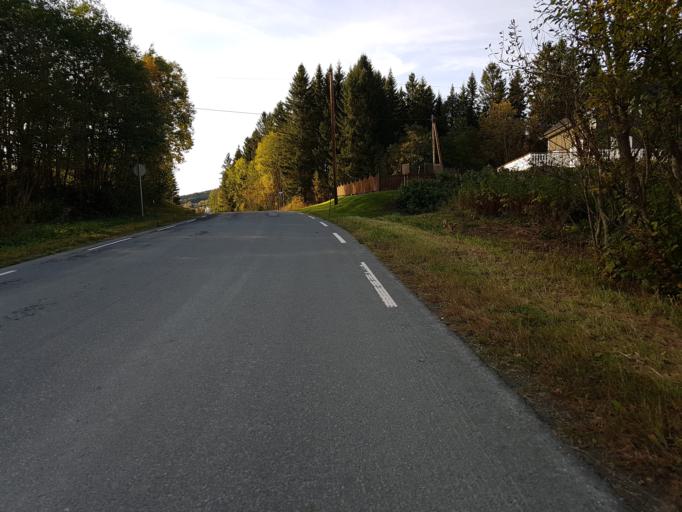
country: NO
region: Sor-Trondelag
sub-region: Klaebu
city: Klaebu
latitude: 63.3474
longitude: 10.5107
